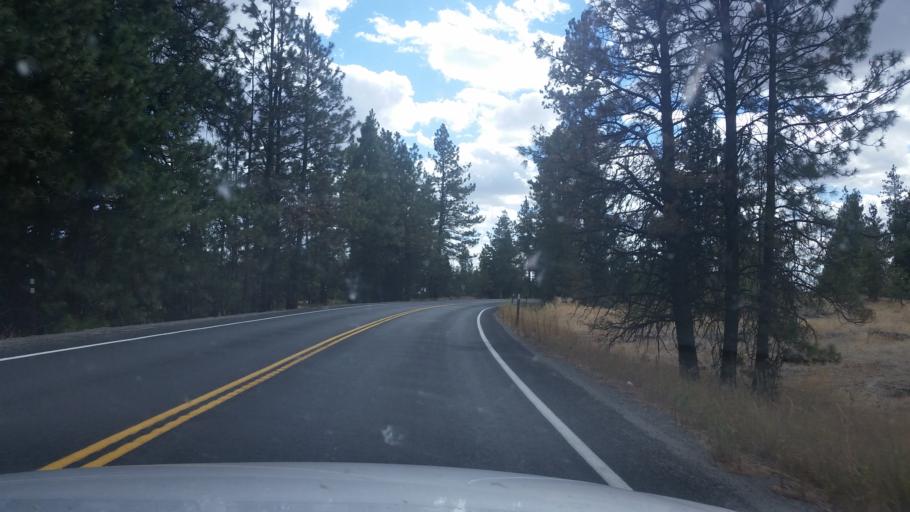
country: US
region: Washington
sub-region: Spokane County
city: Medical Lake
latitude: 47.5441
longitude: -117.7047
